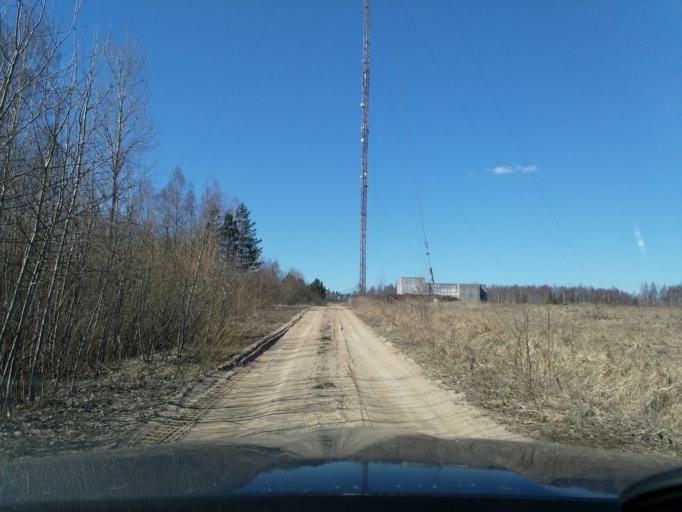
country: LV
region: Kuldigas Rajons
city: Kuldiga
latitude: 56.9344
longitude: 21.9196
